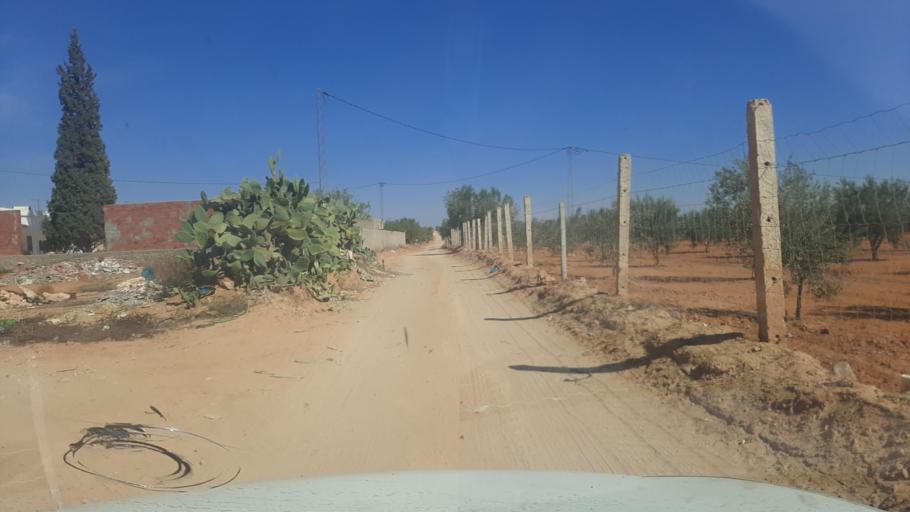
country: TN
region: Safaqis
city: Sfax
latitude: 34.8718
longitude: 10.5621
